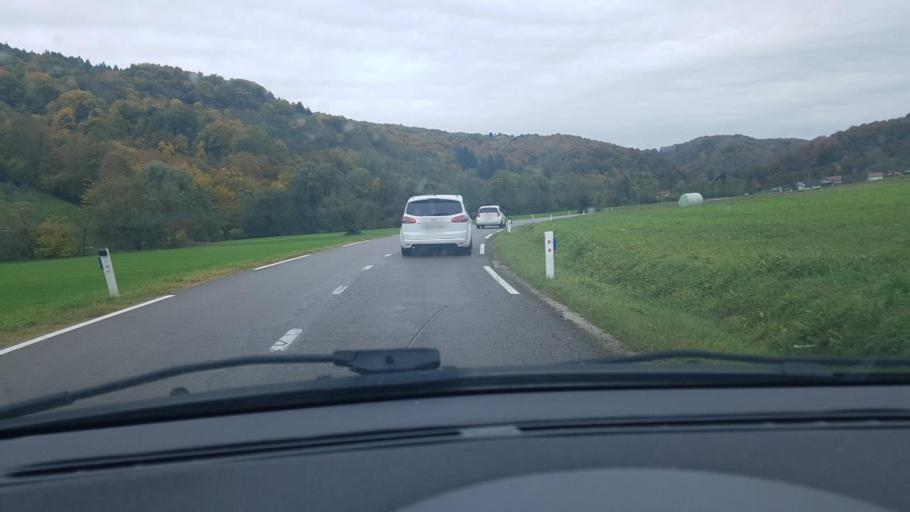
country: SI
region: Majsperk
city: Majsperk
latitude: 46.3332
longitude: 15.7333
